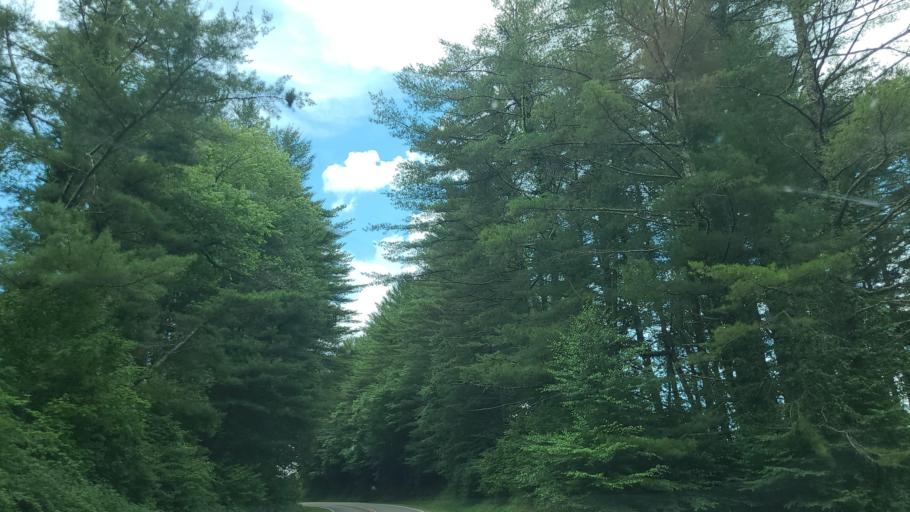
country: US
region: North Carolina
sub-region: Alleghany County
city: Sparta
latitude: 36.4061
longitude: -81.2617
